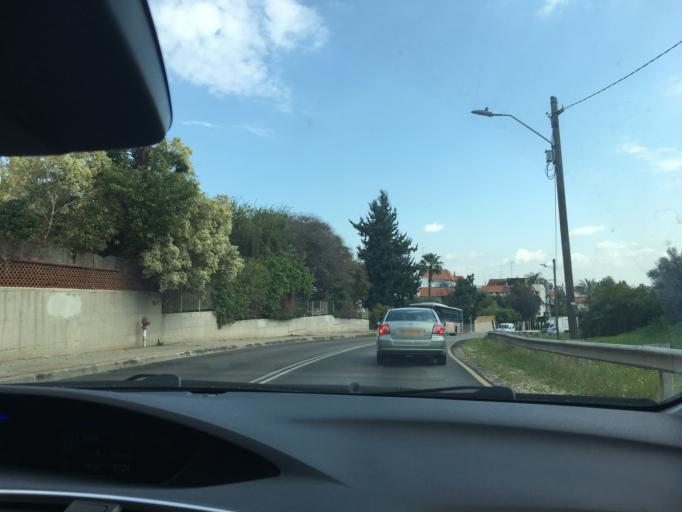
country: IL
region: Tel Aviv
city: Ramat HaSharon
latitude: 32.1613
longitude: 34.8504
